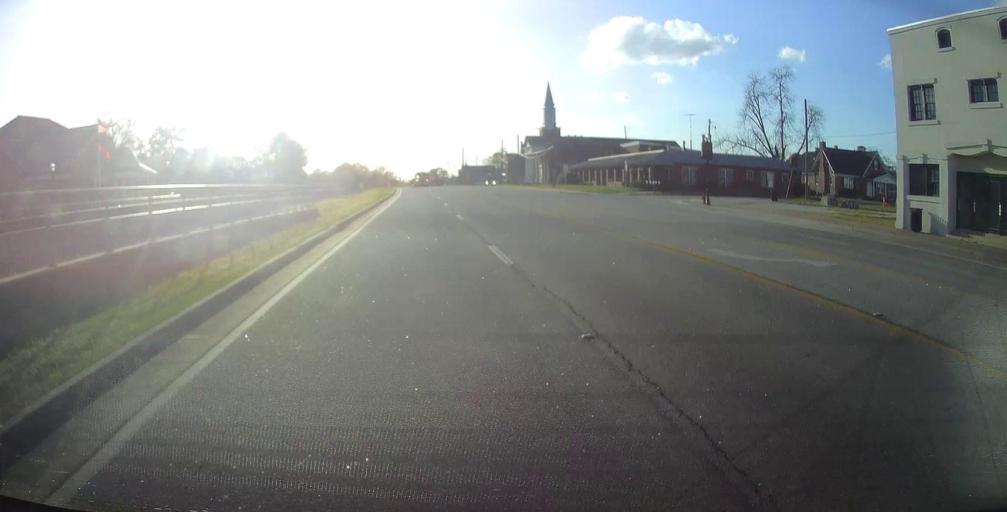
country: US
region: Georgia
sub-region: Evans County
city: Claxton
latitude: 32.1611
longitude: -81.9085
